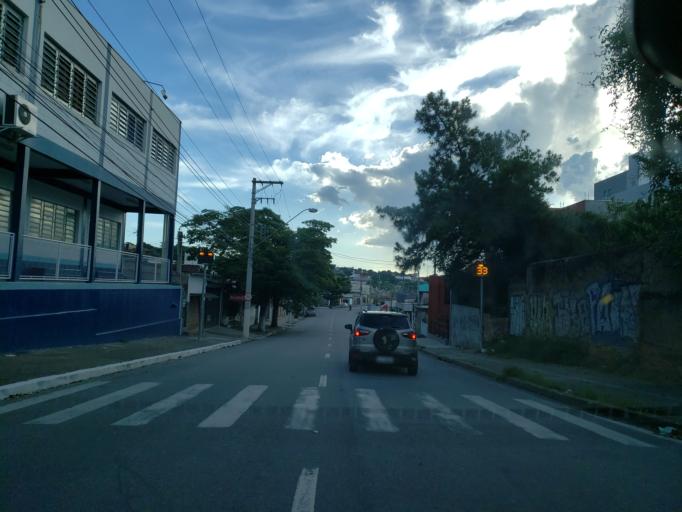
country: BR
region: Sao Paulo
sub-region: Taubate
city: Taubate
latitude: -23.0384
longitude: -45.5690
